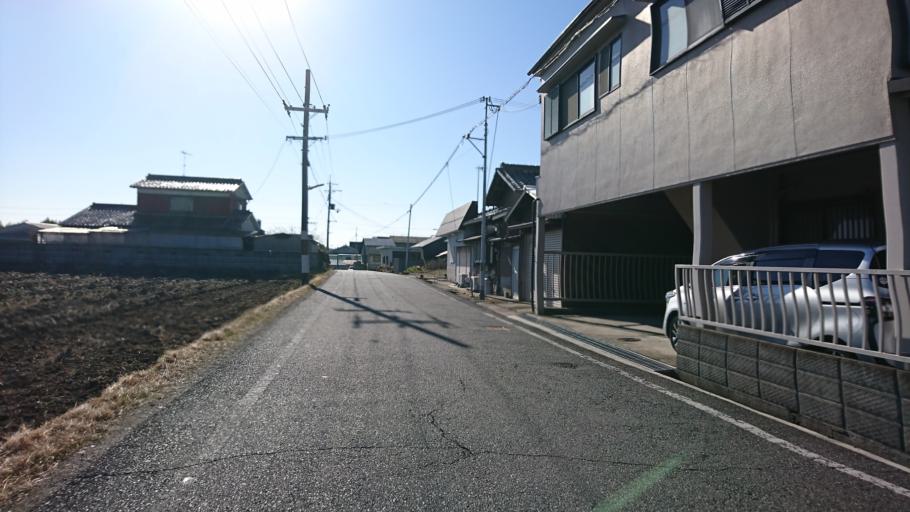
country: JP
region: Hyogo
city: Miki
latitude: 34.7323
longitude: 134.9489
